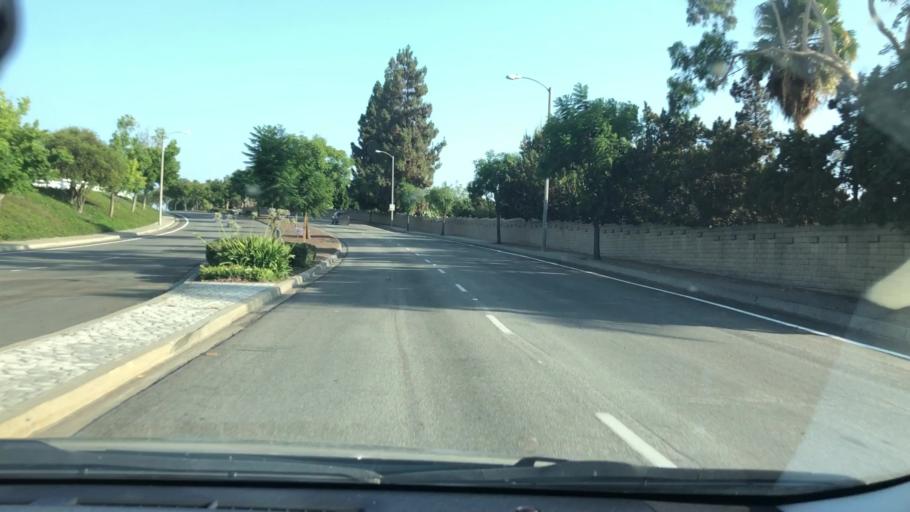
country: US
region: California
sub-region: Orange County
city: Yorba Linda
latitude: 33.8746
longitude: -117.7837
